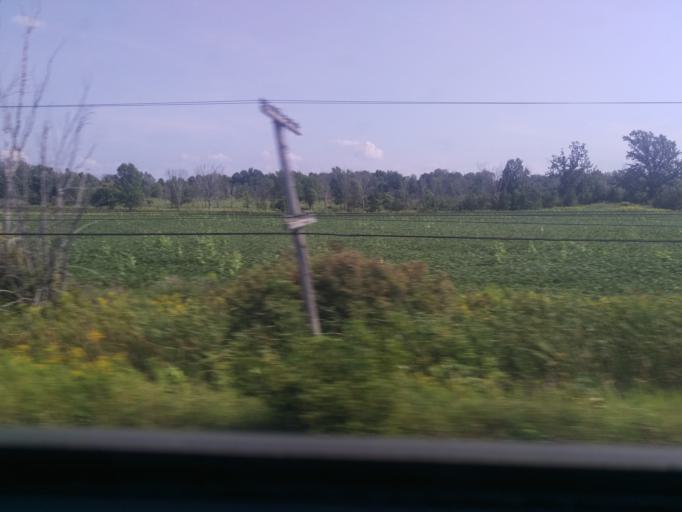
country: US
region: New York
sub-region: Jefferson County
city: Alexandria Bay
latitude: 44.4733
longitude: -75.8929
